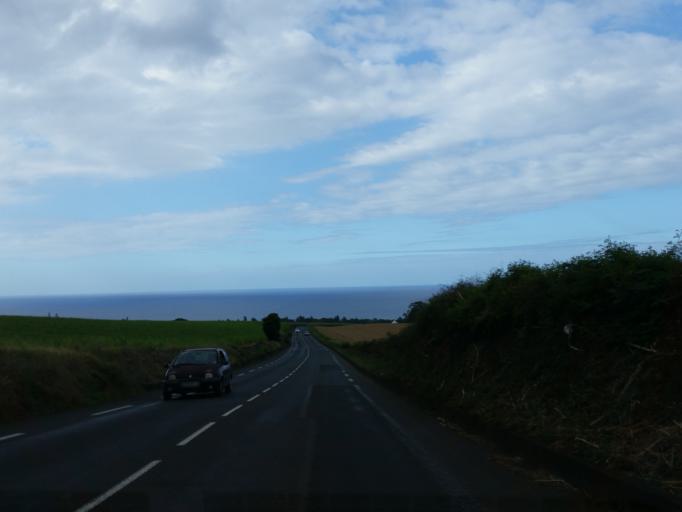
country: RE
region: Reunion
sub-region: Reunion
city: Sainte-Marie
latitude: -20.9129
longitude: 55.5414
